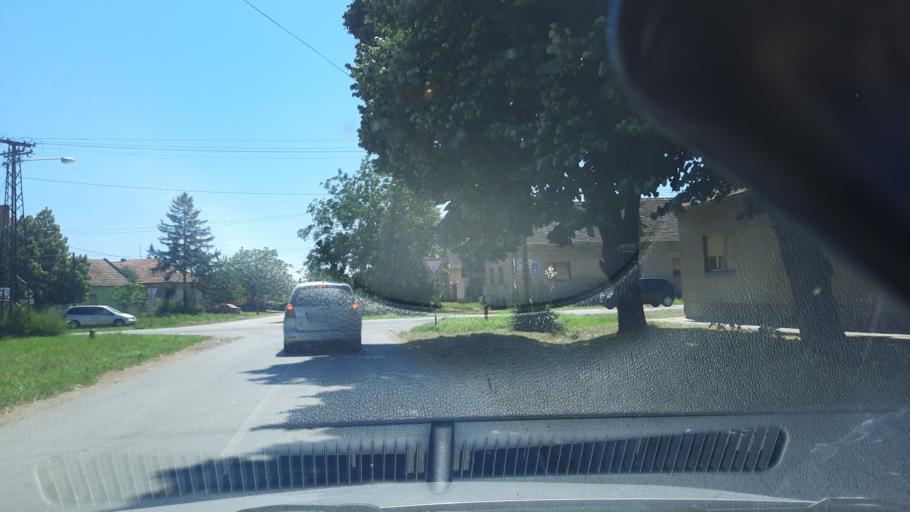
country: RS
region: Autonomna Pokrajina Vojvodina
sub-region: Juznobanatski Okrug
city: Kovin
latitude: 44.7472
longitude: 20.9697
